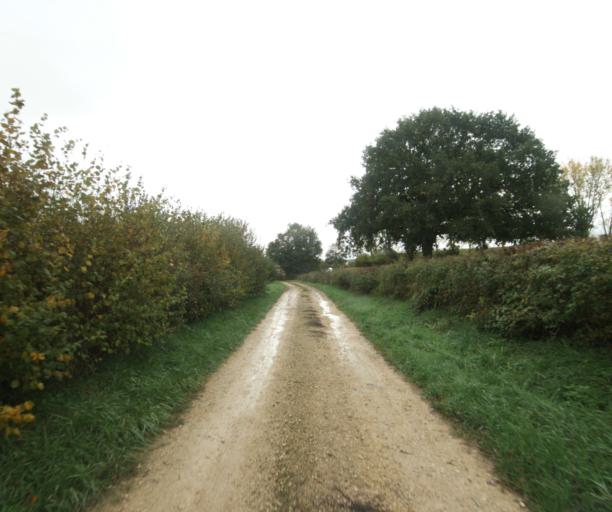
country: FR
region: Rhone-Alpes
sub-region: Departement de l'Ain
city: Pont-de-Vaux
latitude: 46.4822
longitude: 4.8763
